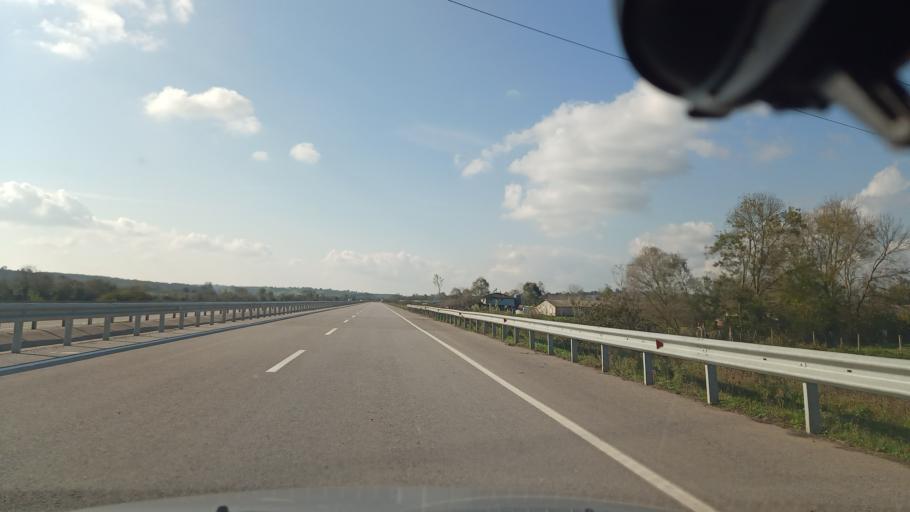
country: TR
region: Sakarya
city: Kaynarca
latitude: 41.0786
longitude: 30.4090
